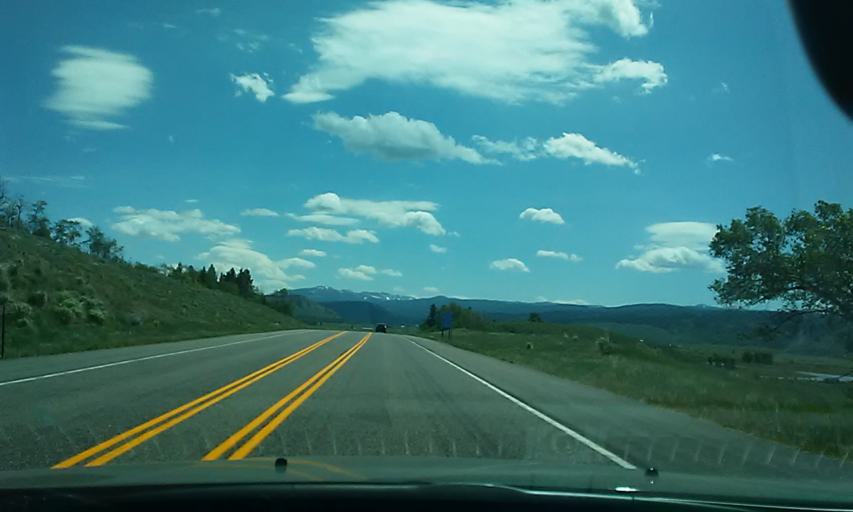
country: US
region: Wyoming
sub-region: Teton County
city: Jackson
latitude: 43.8389
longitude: -110.4473
